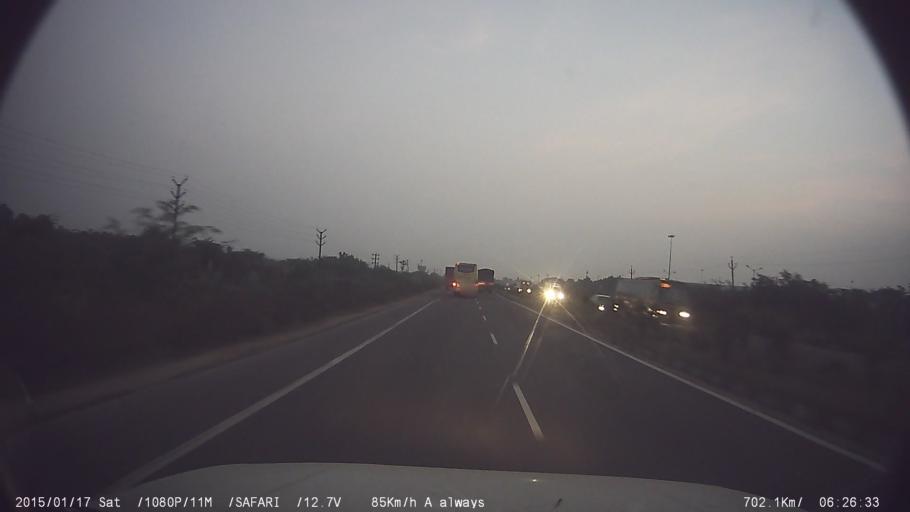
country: IN
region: Tamil Nadu
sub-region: Kancheepuram
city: Sriperumbudur
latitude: 12.9269
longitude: 79.8898
